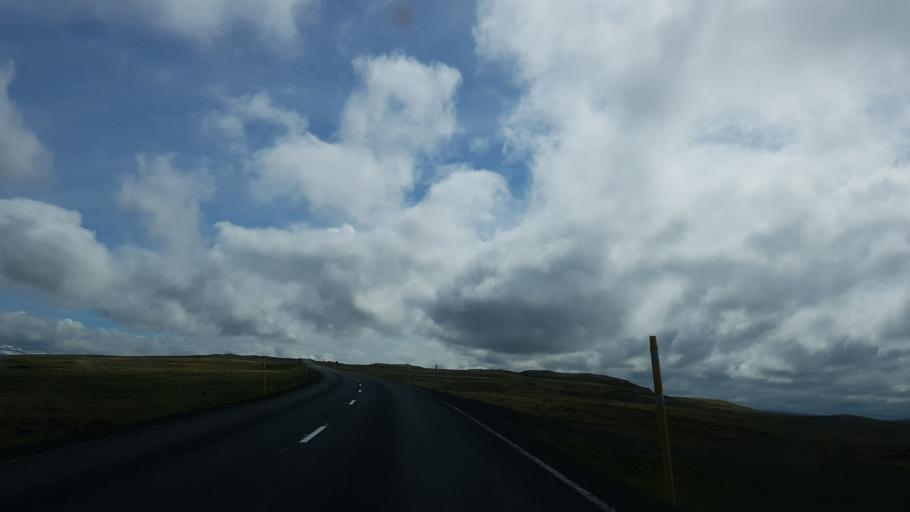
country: IS
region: West
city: Borgarnes
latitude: 64.9977
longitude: -21.0679
